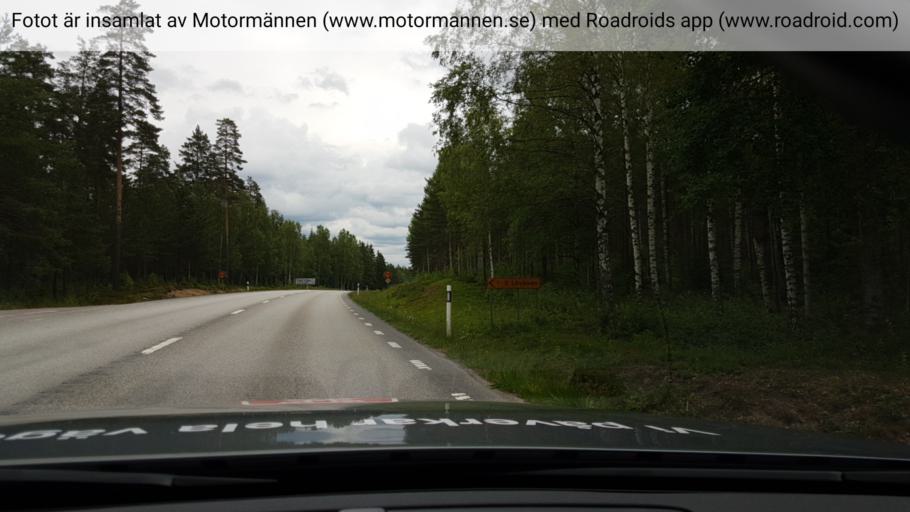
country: SE
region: OErebro
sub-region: Lindesbergs Kommun
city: Lindesberg
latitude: 59.6181
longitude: 15.1938
